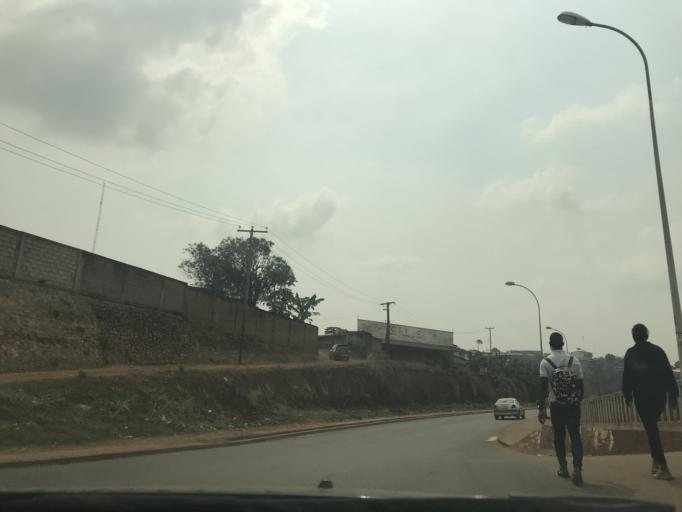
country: CM
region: Centre
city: Yaounde
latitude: 3.8339
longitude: 11.5150
